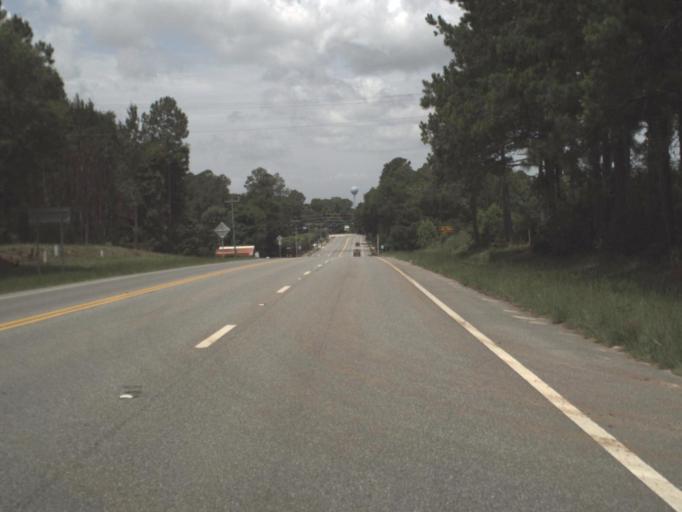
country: US
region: Florida
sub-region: Madison County
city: Madison
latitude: 30.4696
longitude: -83.6220
